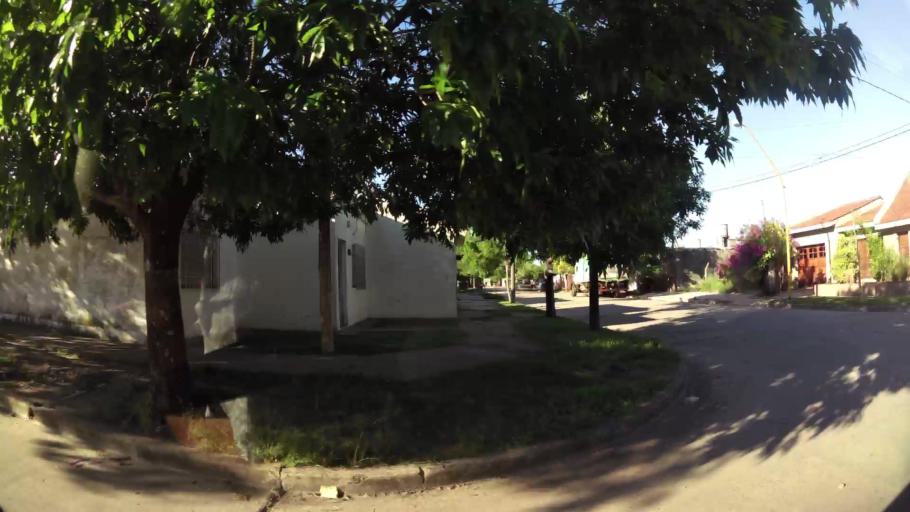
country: AR
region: Cordoba
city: San Francisco
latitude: -31.4434
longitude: -62.0994
